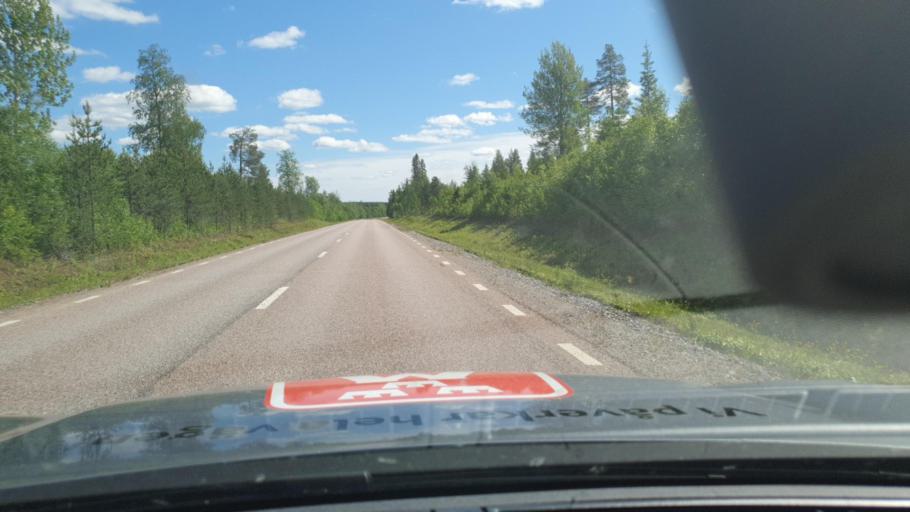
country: FI
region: Lapland
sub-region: Tunturi-Lappi
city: Kolari
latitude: 67.1116
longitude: 23.6274
